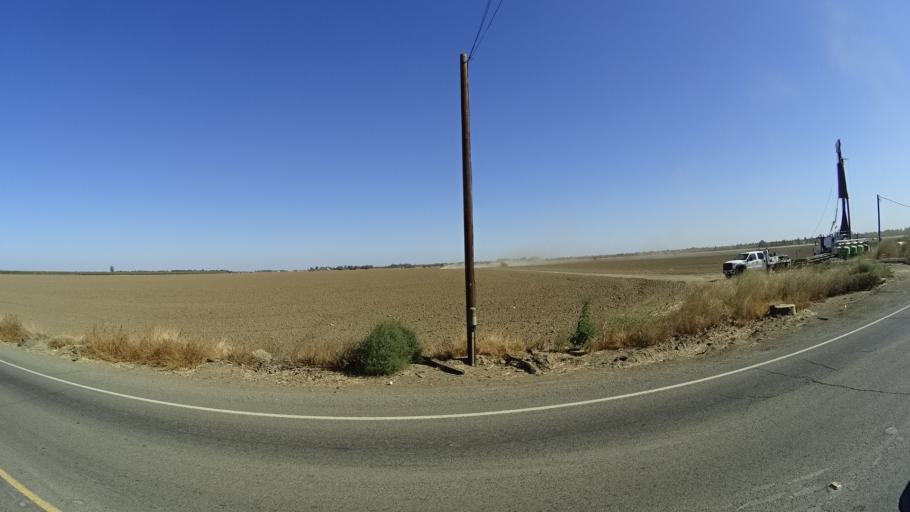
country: US
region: California
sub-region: Yolo County
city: Davis
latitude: 38.5691
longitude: -121.8032
